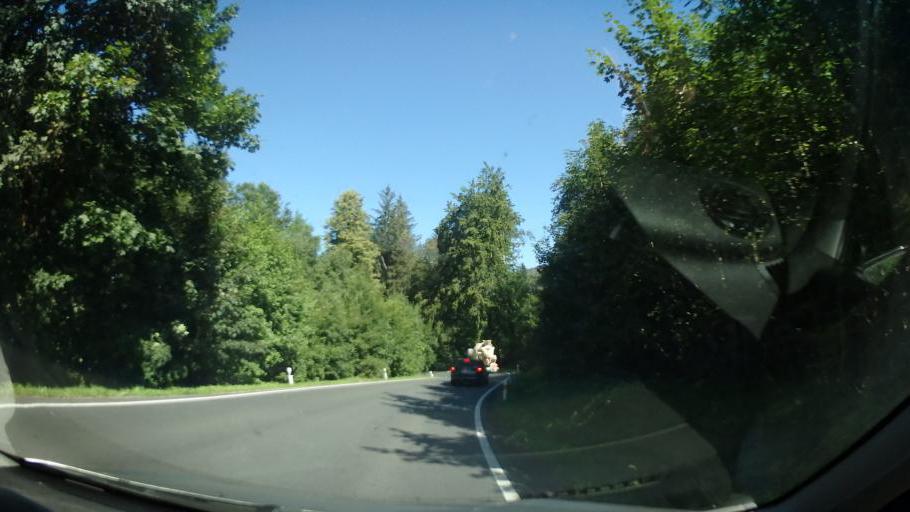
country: CZ
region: Olomoucky
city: Vapenna
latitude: 50.2453
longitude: 17.1415
